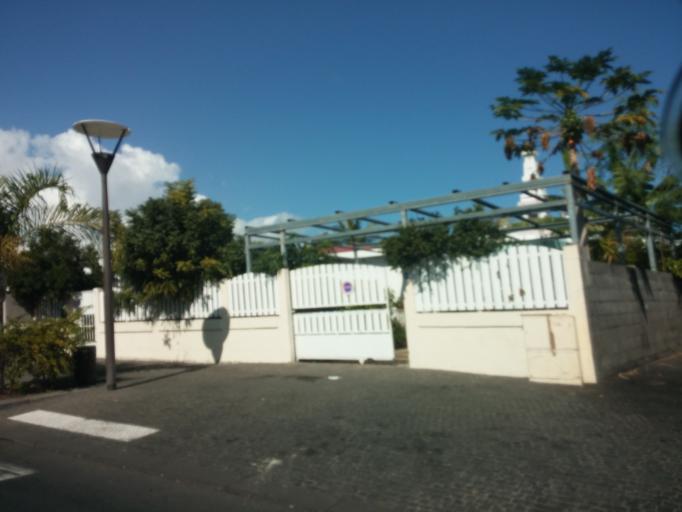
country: RE
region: Reunion
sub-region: Reunion
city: Le Port
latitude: -20.9395
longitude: 55.2932
